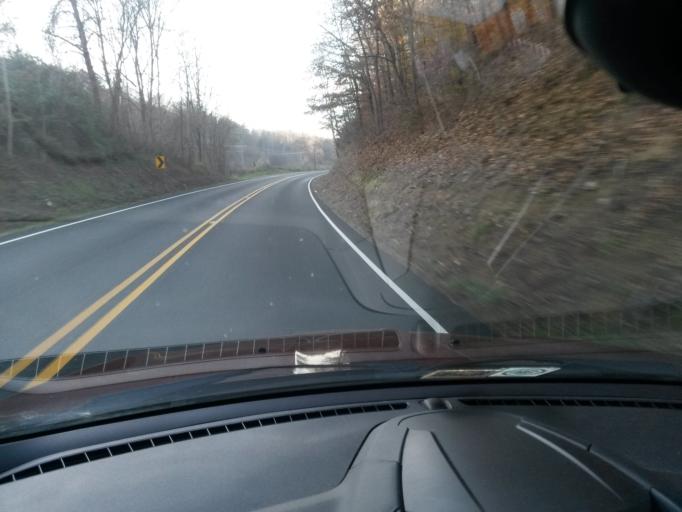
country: US
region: Virginia
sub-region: Amherst County
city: Amherst
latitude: 37.6595
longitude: -79.1523
